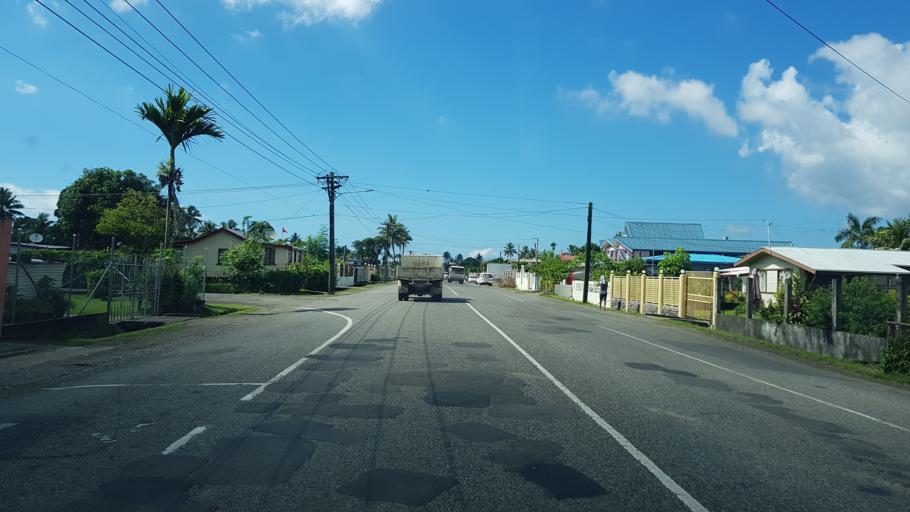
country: FJ
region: Central
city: Suva
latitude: -18.1295
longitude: 178.4593
